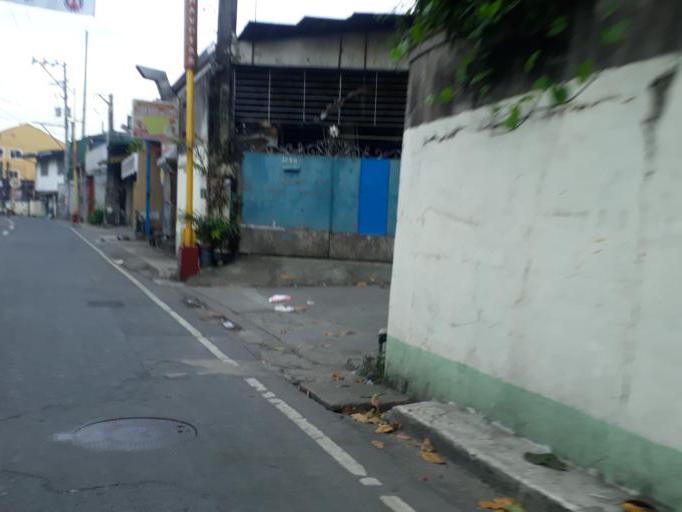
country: PH
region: Calabarzon
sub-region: Province of Rizal
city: Malabon
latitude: 14.6690
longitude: 120.9425
